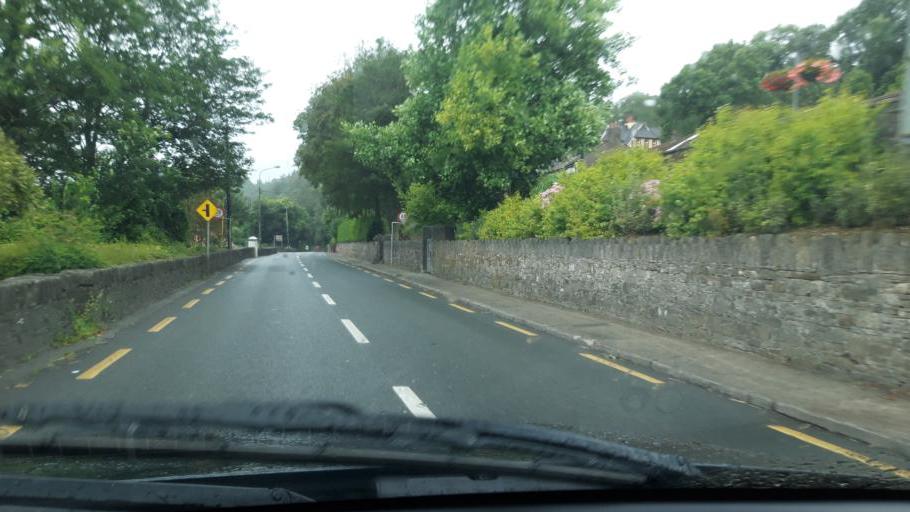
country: IE
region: Munster
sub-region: County Cork
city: Youghal
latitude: 52.1482
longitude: -7.8533
